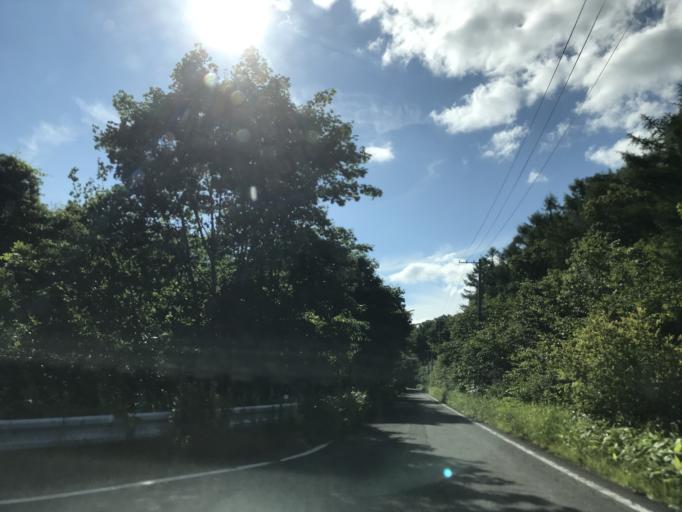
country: JP
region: Iwate
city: Ichinoseki
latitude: 38.9035
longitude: 140.8662
